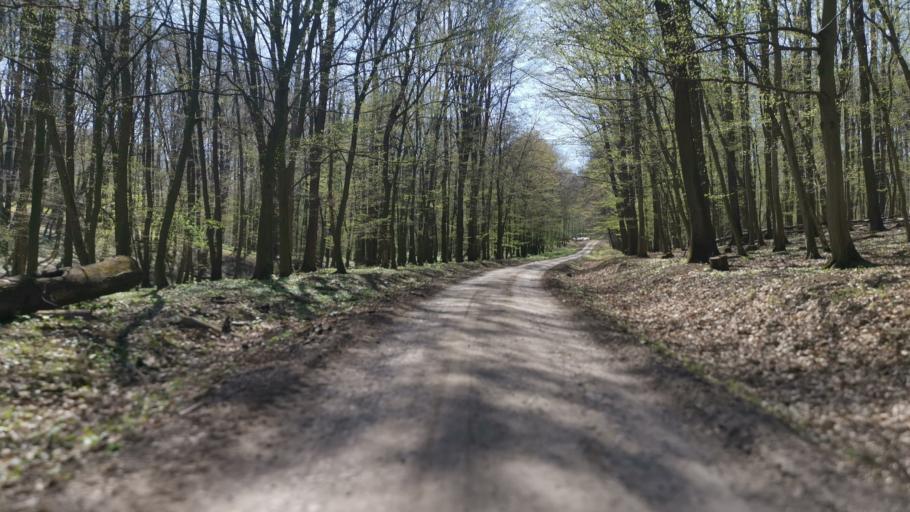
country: SK
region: Trnavsky
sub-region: Okres Senica
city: Senica
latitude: 48.7415
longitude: 17.2735
